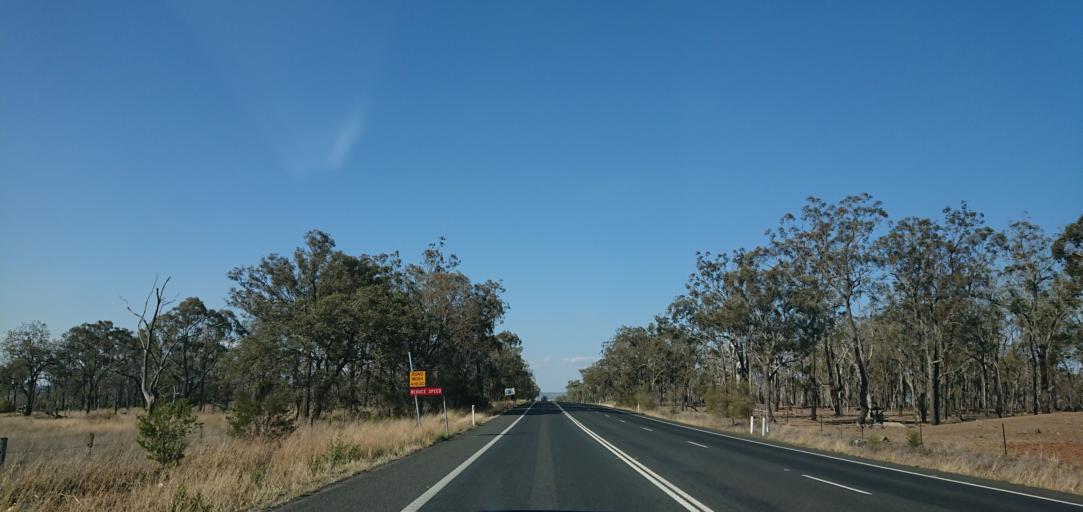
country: AU
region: Queensland
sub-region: Toowoomba
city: Westbrook
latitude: -27.6243
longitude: 151.7616
